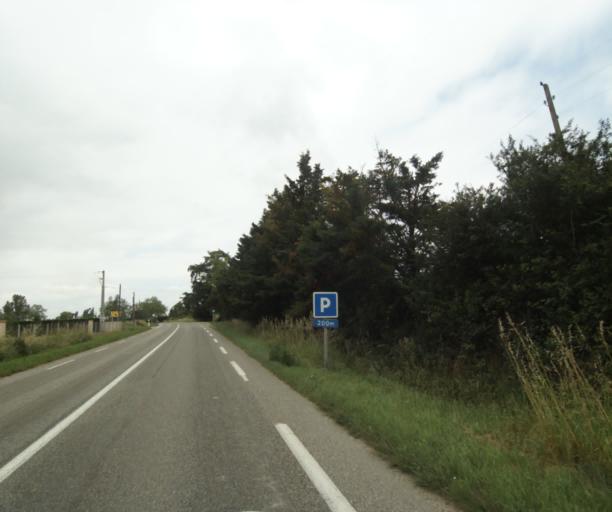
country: FR
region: Midi-Pyrenees
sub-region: Departement du Tarn-et-Garonne
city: Saint-Nauphary
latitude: 43.9722
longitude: 1.4192
